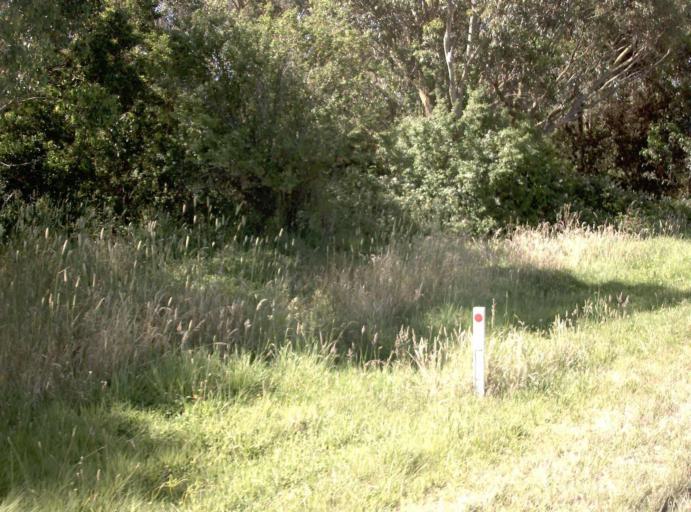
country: AU
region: Victoria
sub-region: Latrobe
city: Morwell
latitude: -38.6600
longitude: 146.4531
